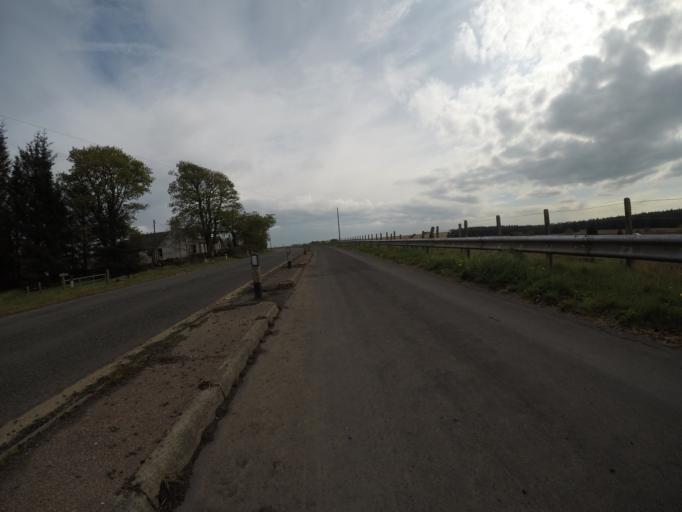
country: GB
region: Scotland
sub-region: East Renfrewshire
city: Neilston
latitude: 55.7100
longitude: -4.3996
